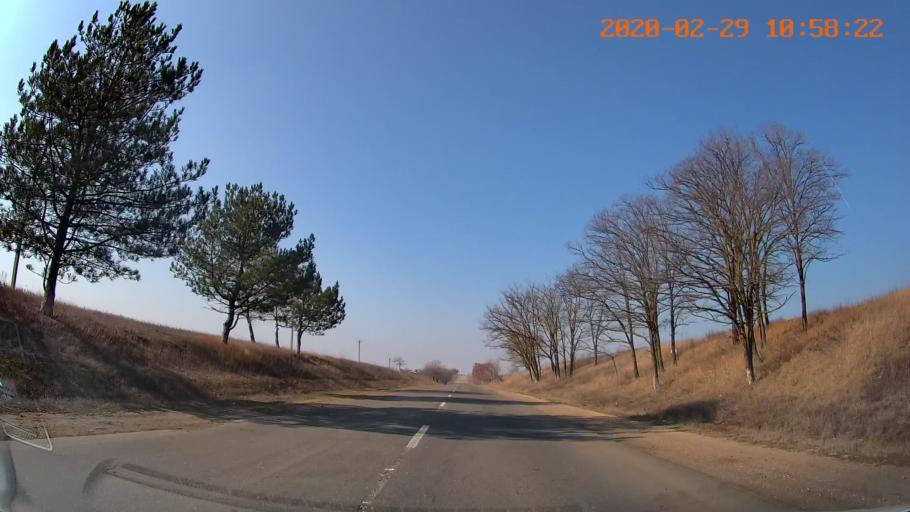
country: MD
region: Telenesti
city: Grigoriopol
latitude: 47.1667
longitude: 29.3119
